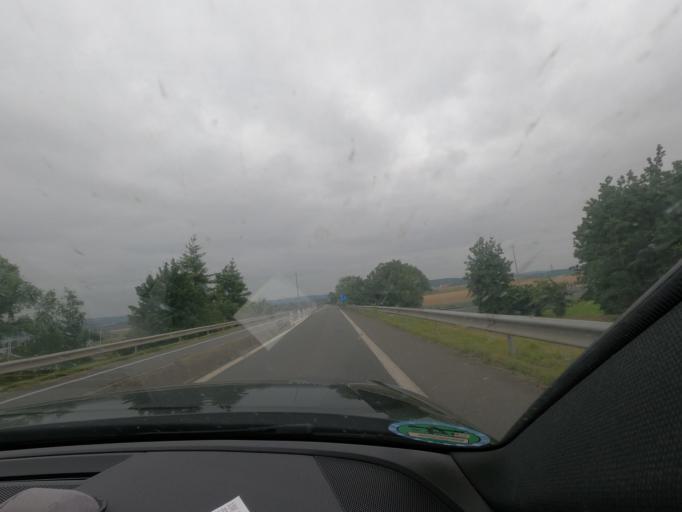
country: FR
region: Picardie
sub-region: Departement de l'Oise
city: Ressons-sur-Matz
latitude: 49.5214
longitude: 2.7197
